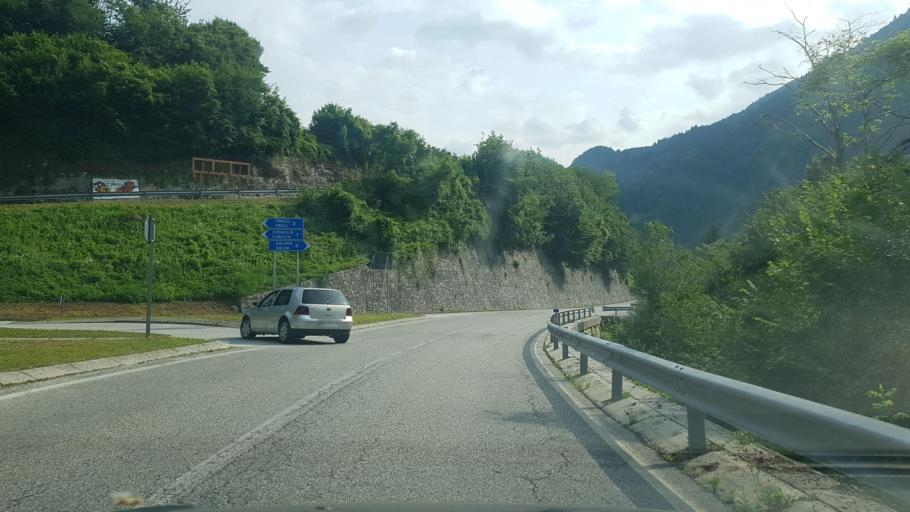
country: IT
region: Friuli Venezia Giulia
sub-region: Provincia di Udine
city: Paularo
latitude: 46.4889
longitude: 13.0986
